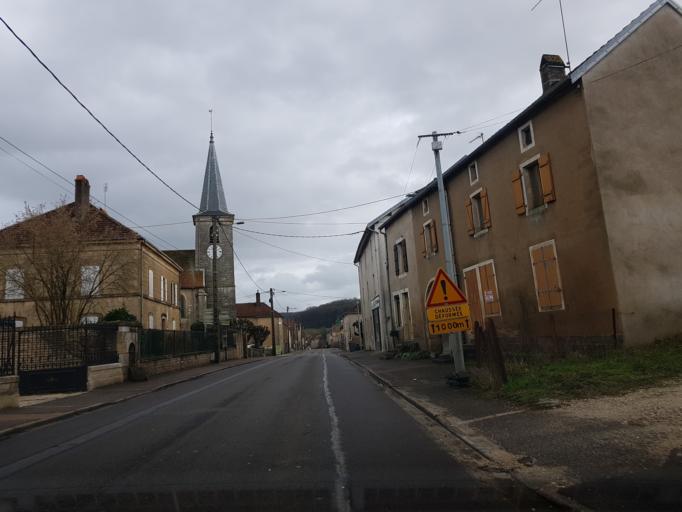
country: FR
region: Franche-Comte
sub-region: Departement de la Haute-Saone
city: Scey-sur-Saone-et-Saint-Albin
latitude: 47.7111
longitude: 5.8893
